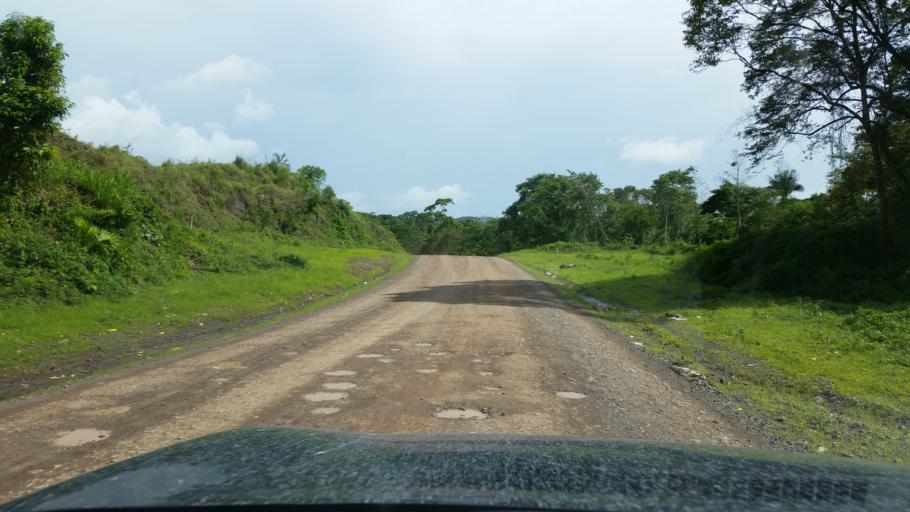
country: NI
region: Atlantico Norte (RAAN)
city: Siuna
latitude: 13.6537
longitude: -84.7936
